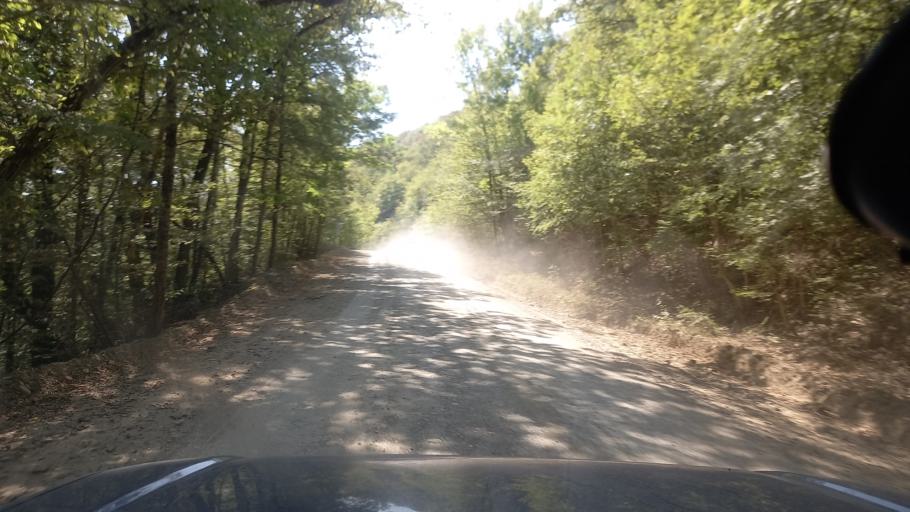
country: RU
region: Krasnodarskiy
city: Azovskaya
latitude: 44.6921
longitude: 38.6380
